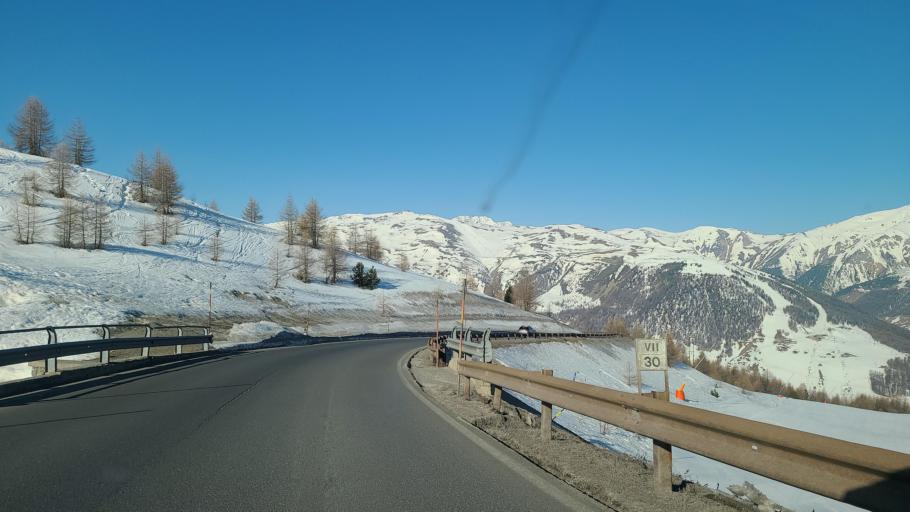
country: IT
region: Lombardy
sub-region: Provincia di Sondrio
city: Livigno
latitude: 46.5378
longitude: 10.1629
